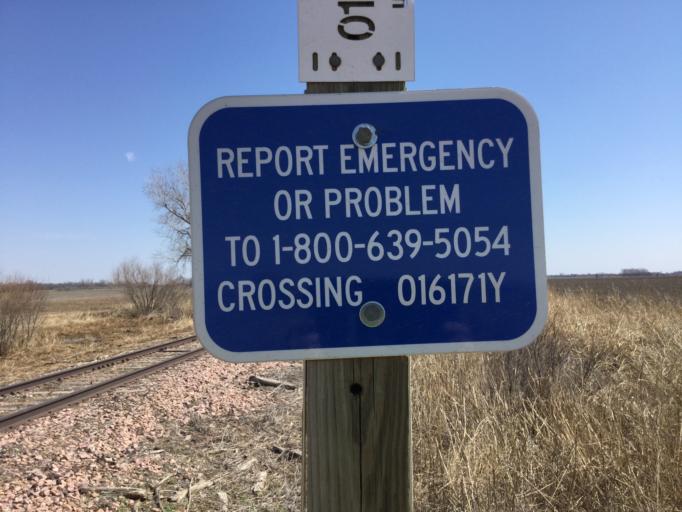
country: US
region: Kansas
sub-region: Barber County
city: Medicine Lodge
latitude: 37.2449
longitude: -98.3855
